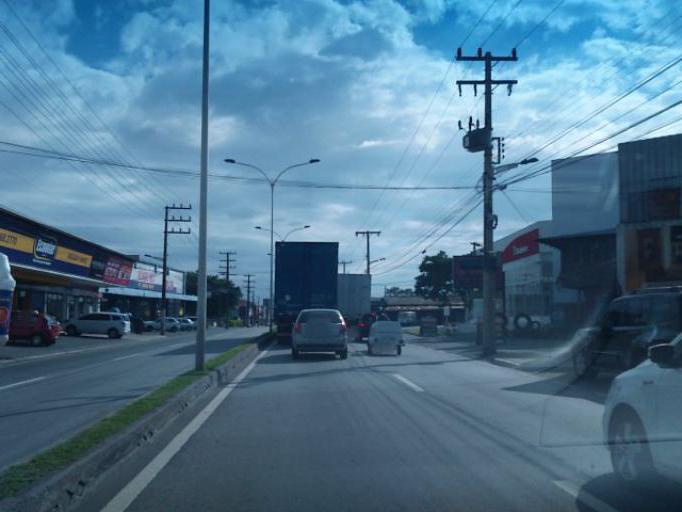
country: BR
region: Santa Catarina
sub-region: Itajai
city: Itajai
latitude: -26.8856
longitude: -48.6969
